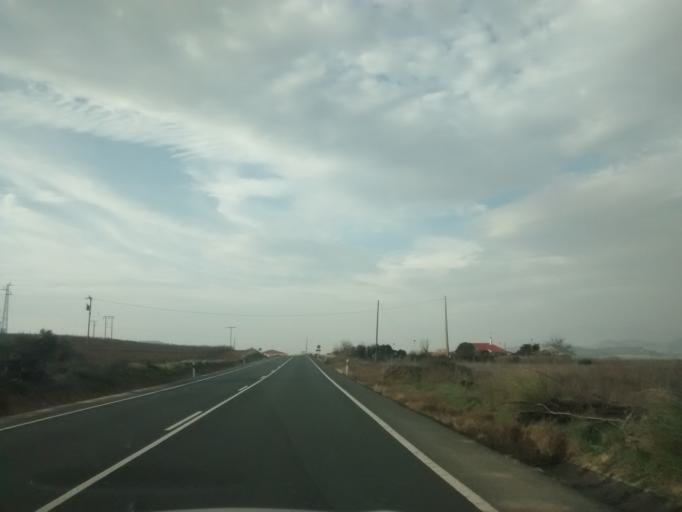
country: ES
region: La Rioja
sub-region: Provincia de La Rioja
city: Torremontalbo
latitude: 42.4942
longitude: -2.6693
